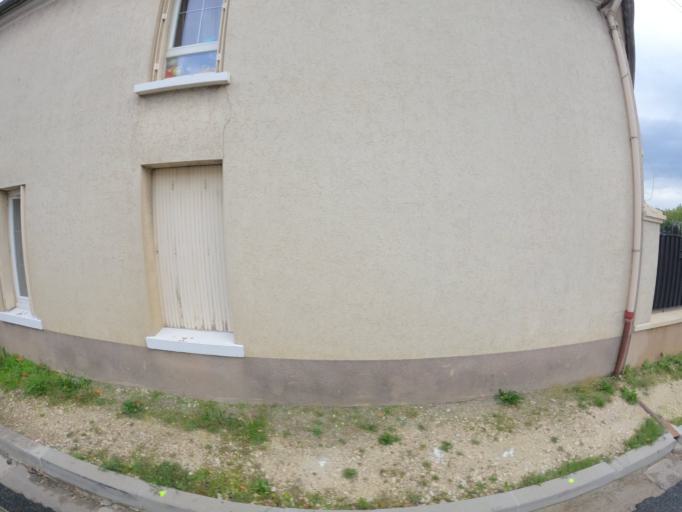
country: FR
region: Ile-de-France
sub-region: Departement de Seine-et-Marne
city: Saint-Germain-sur-Morin
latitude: 48.8809
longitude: 2.8511
